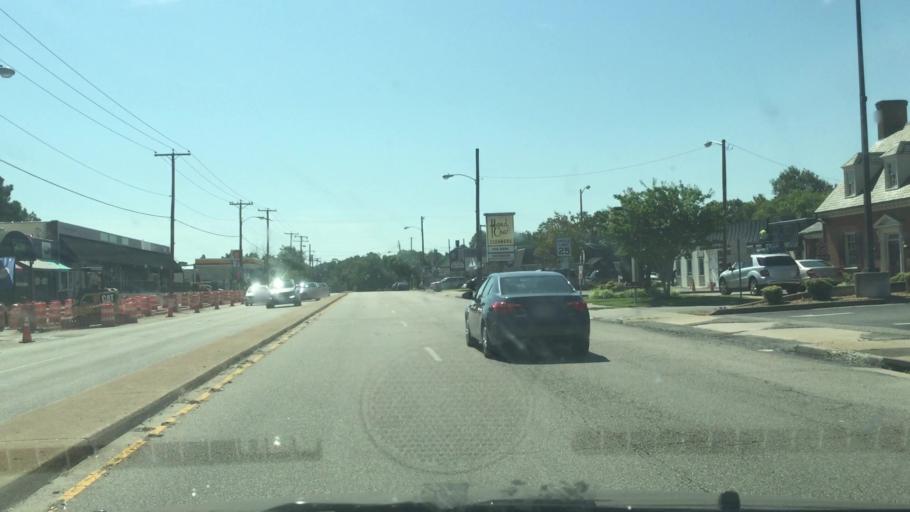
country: US
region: Virginia
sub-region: Henrico County
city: Dumbarton
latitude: 37.5792
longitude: -77.5141
